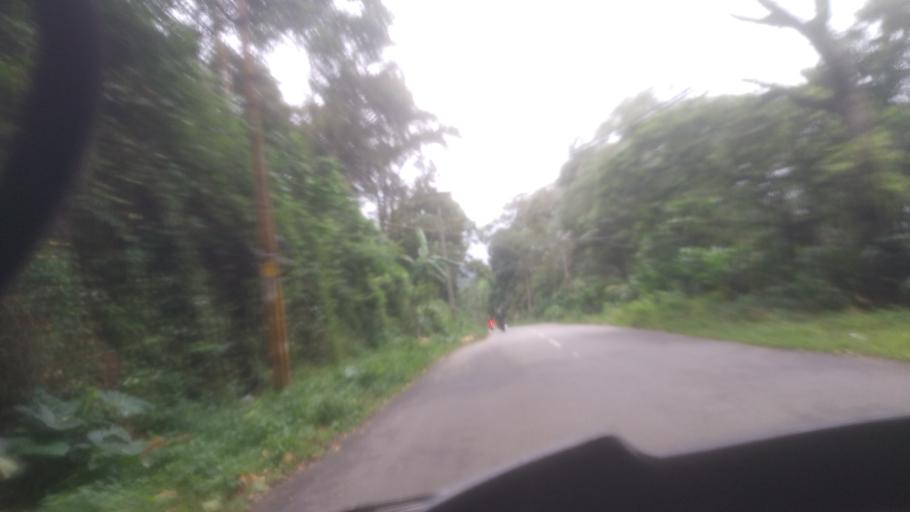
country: IN
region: Tamil Nadu
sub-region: Theni
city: Kombai
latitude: 9.8966
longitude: 77.1931
